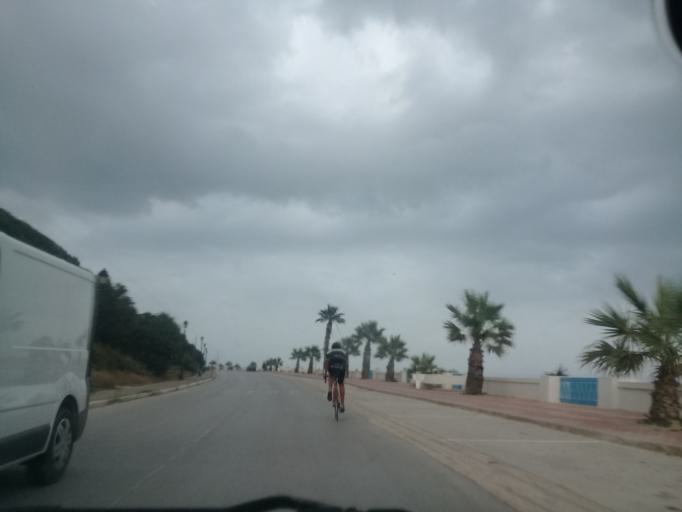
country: TN
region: Tunis
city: Sidi Bou Said
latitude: 36.8652
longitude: 10.3455
